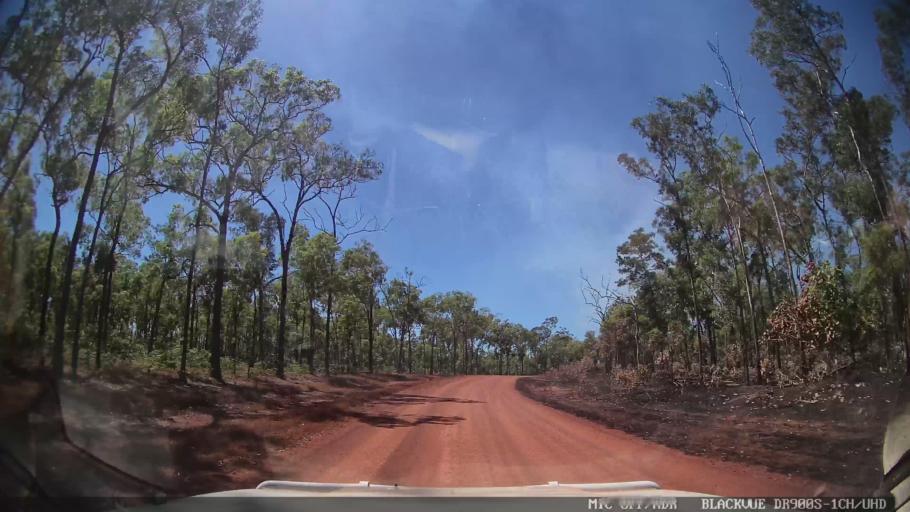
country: AU
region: Queensland
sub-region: Torres
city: Thursday Island
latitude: -10.9697
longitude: 142.3454
